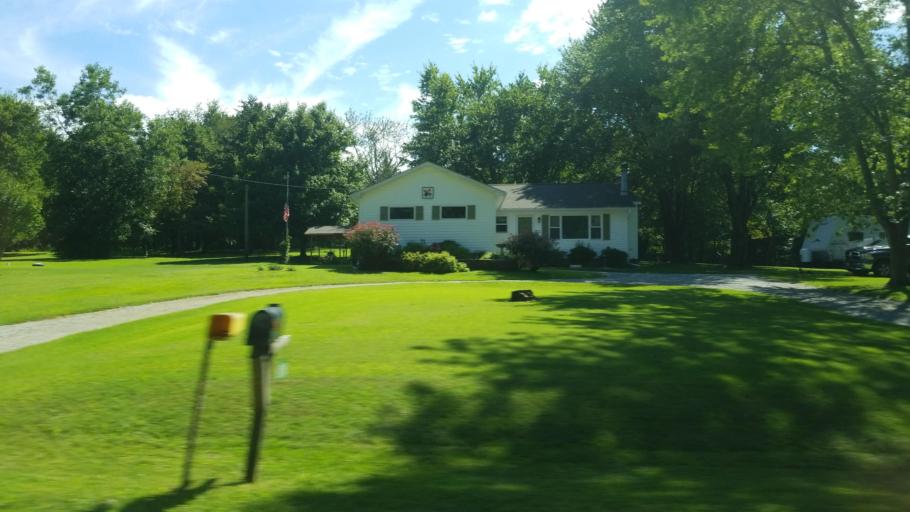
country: US
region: Illinois
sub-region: Williamson County
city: Johnston City
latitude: 37.7892
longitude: -88.9073
